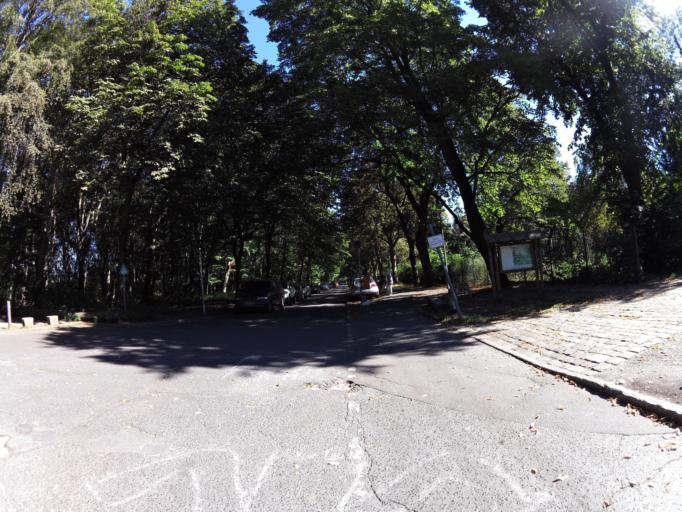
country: DE
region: Berlin
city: Reinickendorf
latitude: 52.5477
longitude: 13.3278
